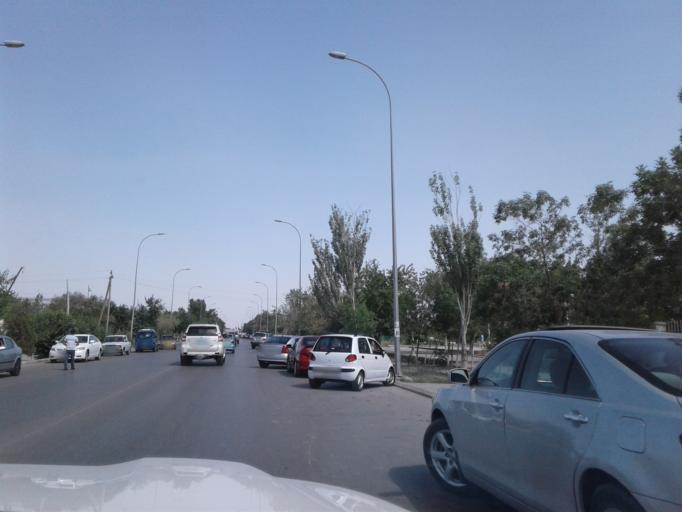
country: TM
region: Dasoguz
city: Dasoguz
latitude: 41.8359
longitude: 59.9688
